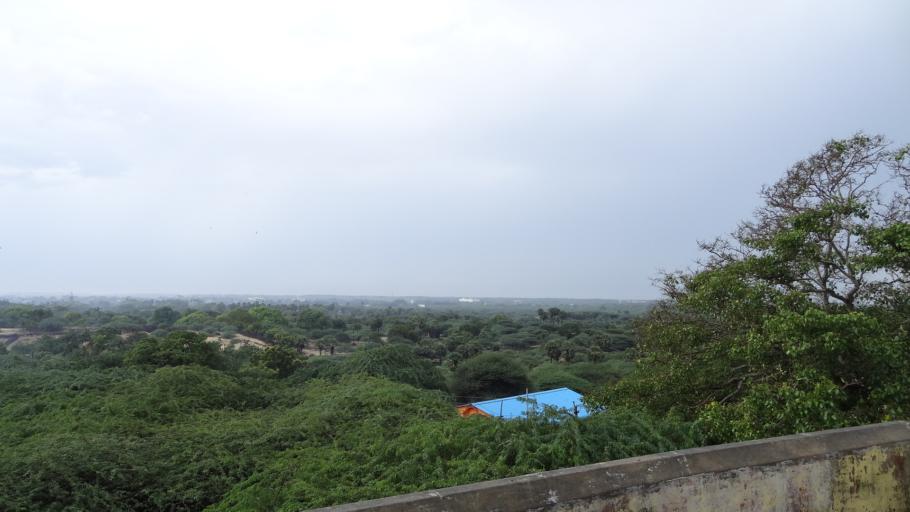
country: IN
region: Tamil Nadu
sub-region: Virudhunagar
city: Rameswaram
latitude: 9.3026
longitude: 79.3054
